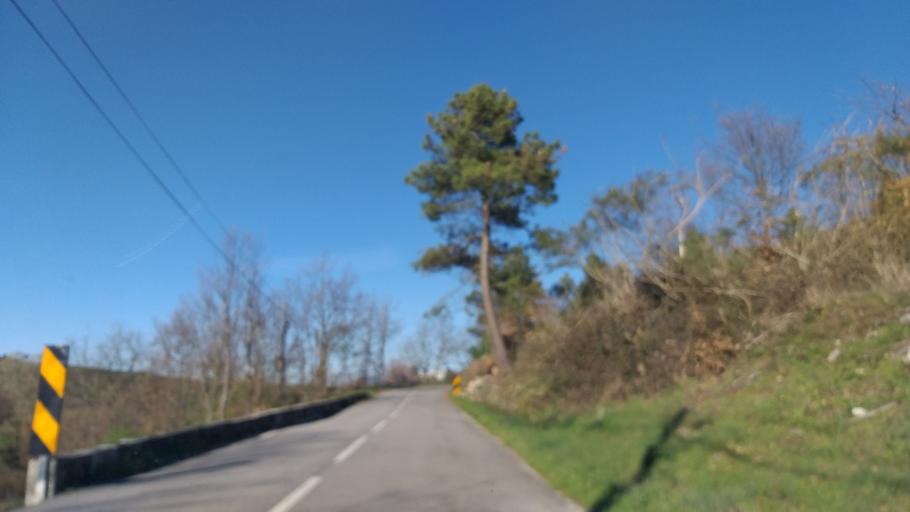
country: PT
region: Guarda
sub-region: Celorico da Beira
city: Celorico da Beira
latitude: 40.5972
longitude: -7.3629
